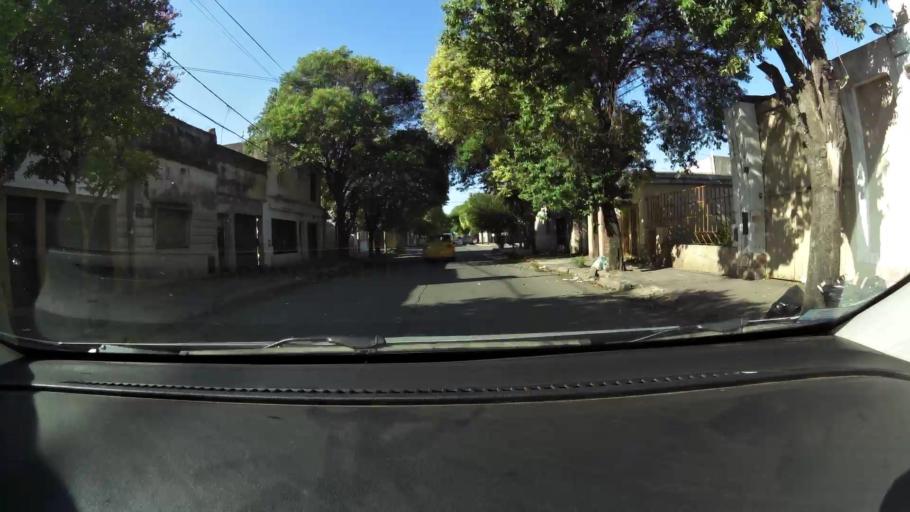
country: AR
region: Cordoba
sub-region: Departamento de Capital
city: Cordoba
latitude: -31.3926
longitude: -64.1718
